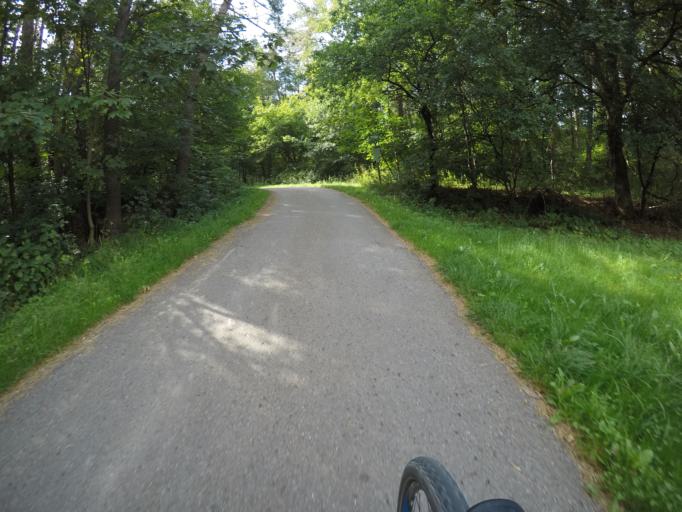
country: DE
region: Baden-Wuerttemberg
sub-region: Karlsruhe Region
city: Althengstett
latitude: 48.7167
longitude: 8.8051
